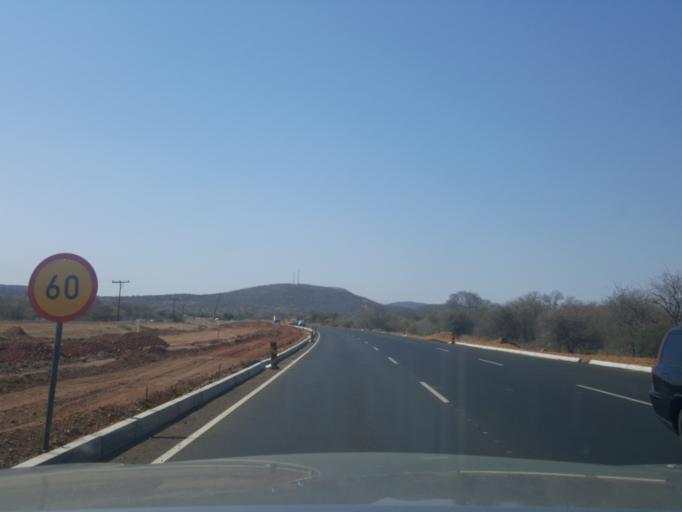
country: BW
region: South East
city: Ramotswa
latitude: -24.7681
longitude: 25.8309
